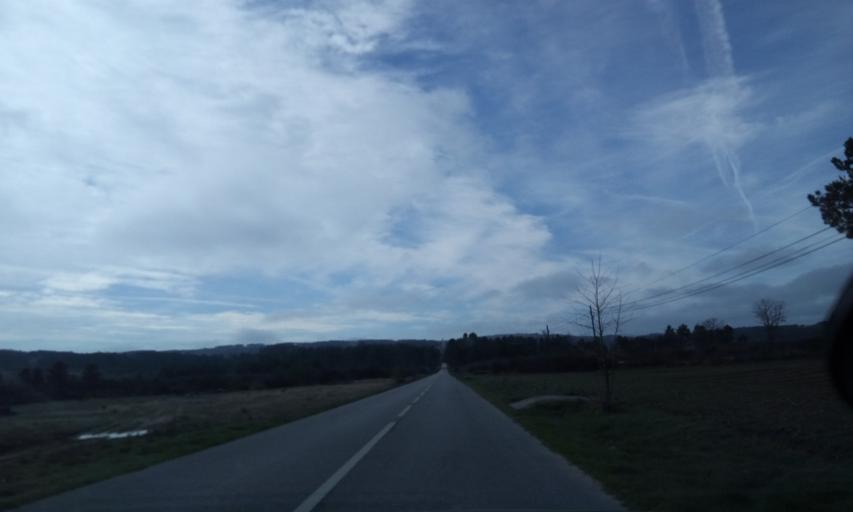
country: PT
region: Guarda
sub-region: Fornos de Algodres
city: Fornos de Algodres
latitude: 40.6714
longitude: -7.5288
